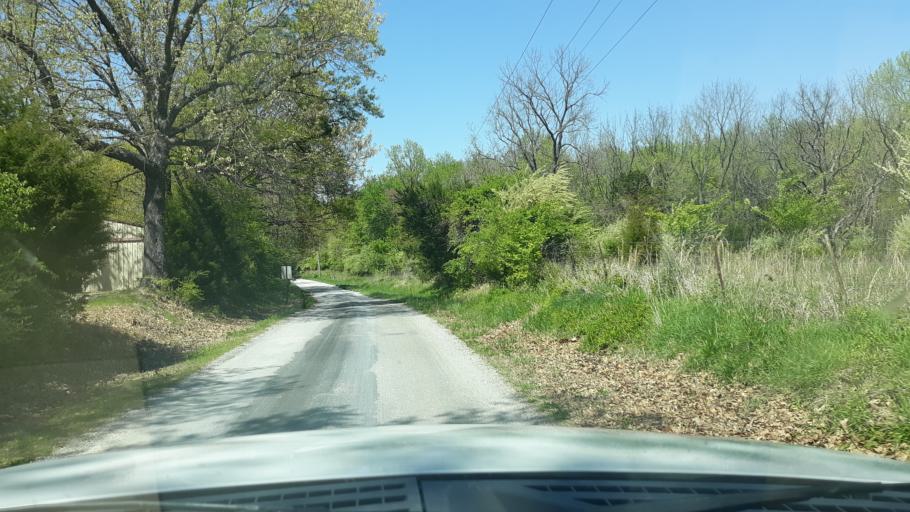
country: US
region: Illinois
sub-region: Saline County
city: Harrisburg
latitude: 37.8625
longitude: -88.6393
